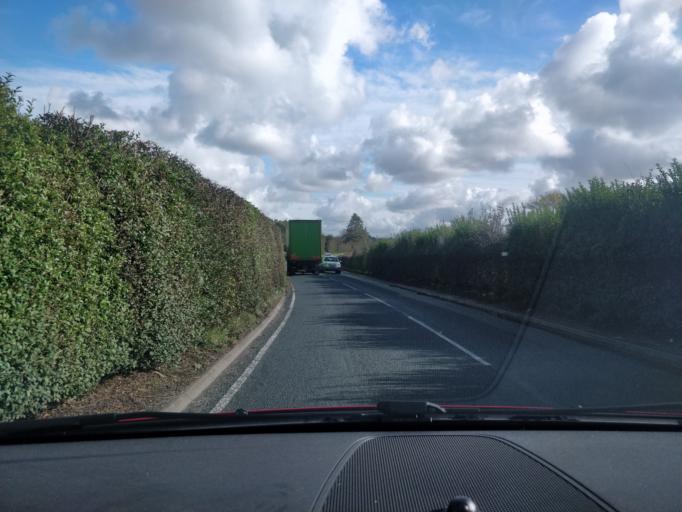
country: GB
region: England
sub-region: Lancashire
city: Ormskirk
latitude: 53.5898
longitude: -2.8779
